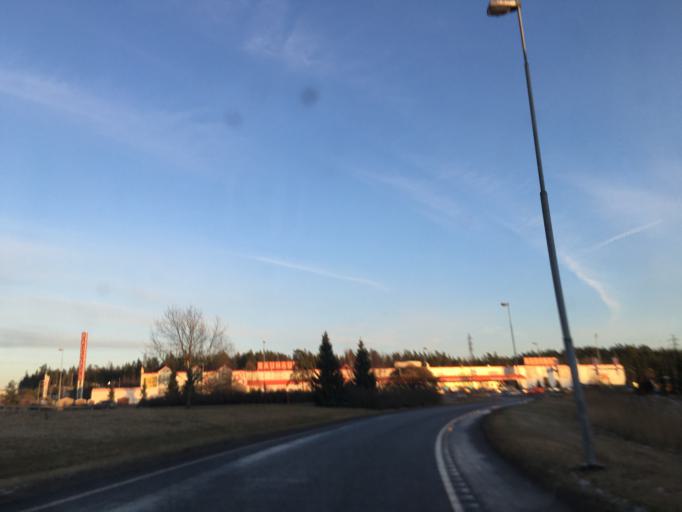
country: FI
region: Varsinais-Suomi
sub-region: Turku
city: Raisio
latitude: 60.4922
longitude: 22.2045
